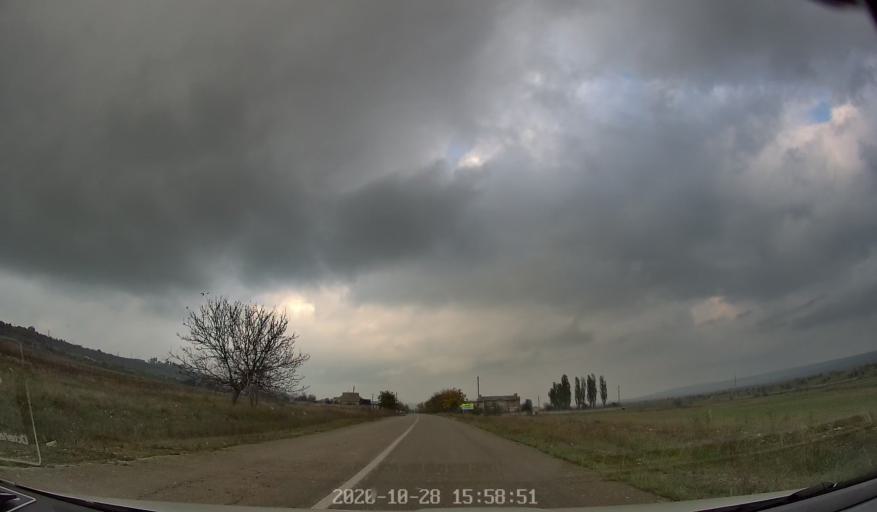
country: UA
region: Odessa
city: Zaliznychne
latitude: 45.7695
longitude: 28.5720
